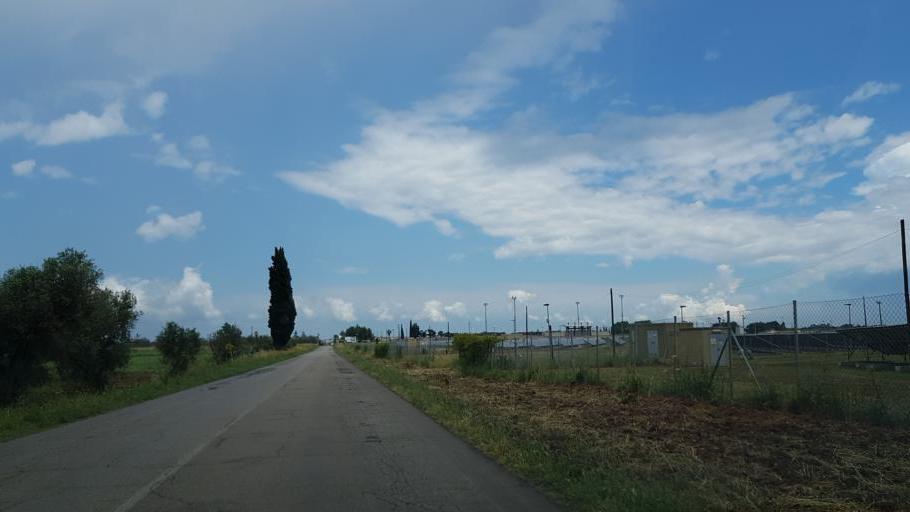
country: IT
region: Apulia
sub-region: Provincia di Brindisi
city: San Donaci
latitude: 40.4418
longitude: 17.9067
